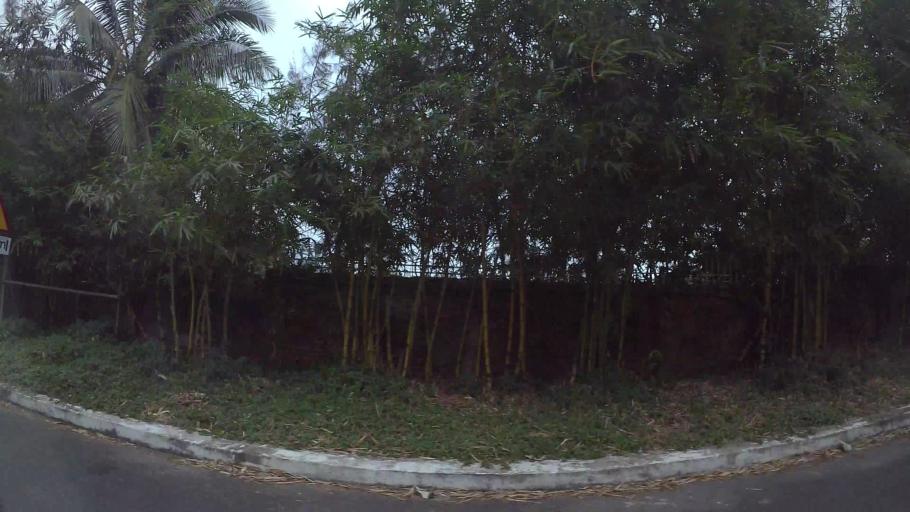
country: VN
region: Da Nang
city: Son Tra
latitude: 16.1063
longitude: 108.2944
